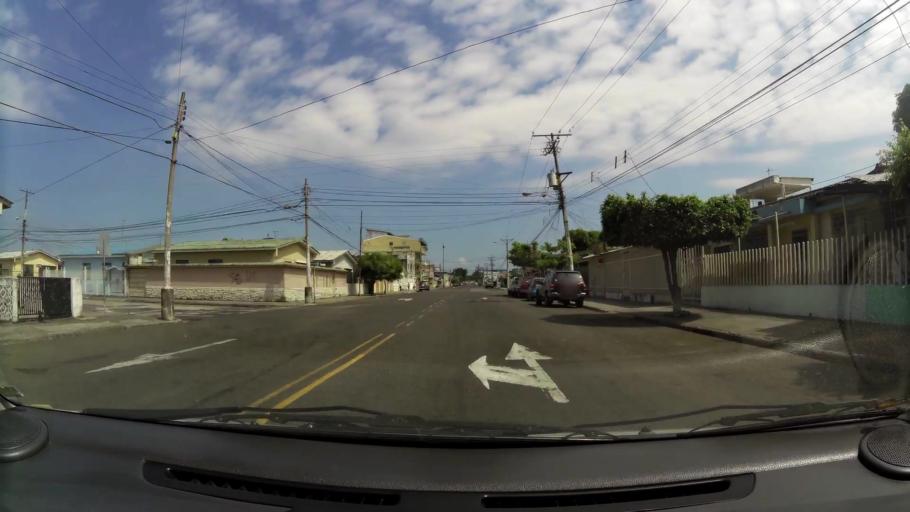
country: EC
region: Guayas
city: Guayaquil
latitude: -2.2317
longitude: -79.8927
